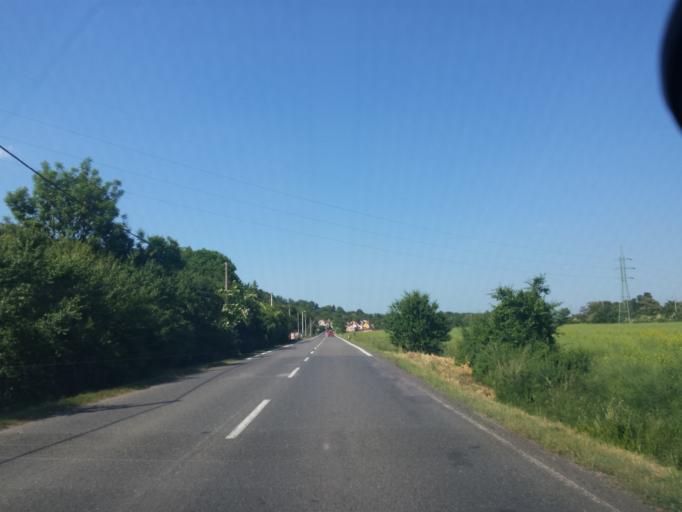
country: CZ
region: Central Bohemia
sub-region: Okres Melnik
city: Veltrusy
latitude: 50.2949
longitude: 14.3115
